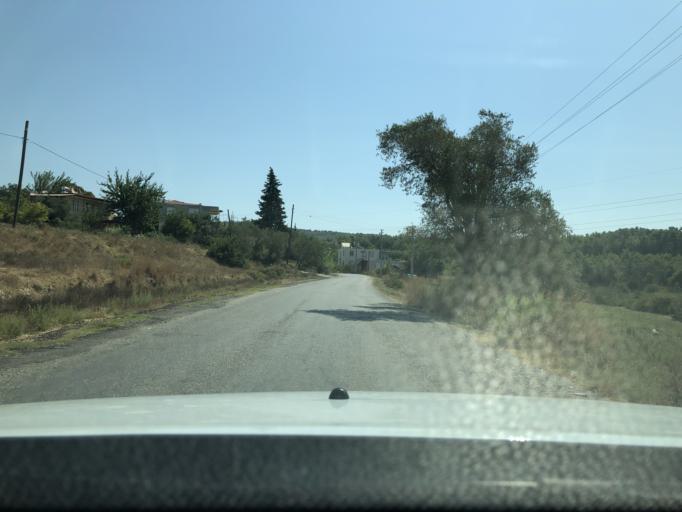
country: TR
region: Antalya
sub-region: Manavgat
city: Manavgat
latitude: 36.8217
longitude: 31.5009
